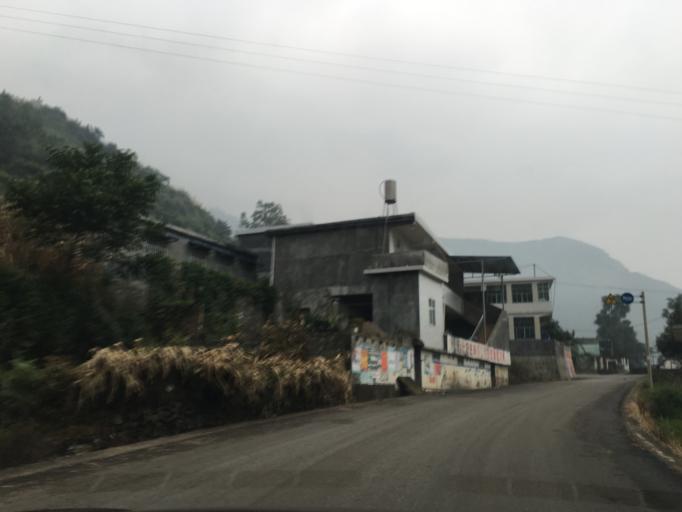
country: CN
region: Guizhou Sheng
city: Liupanshui
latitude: 26.0637
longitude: 105.1357
